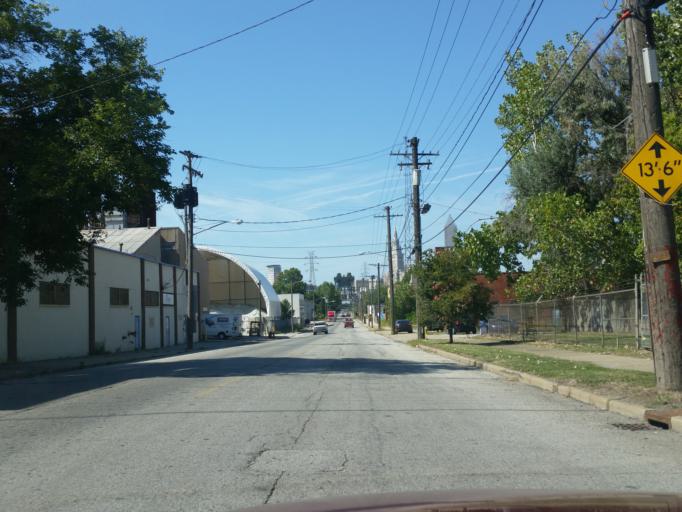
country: US
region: Ohio
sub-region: Cuyahoga County
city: Cleveland
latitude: 41.4823
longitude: -81.6796
